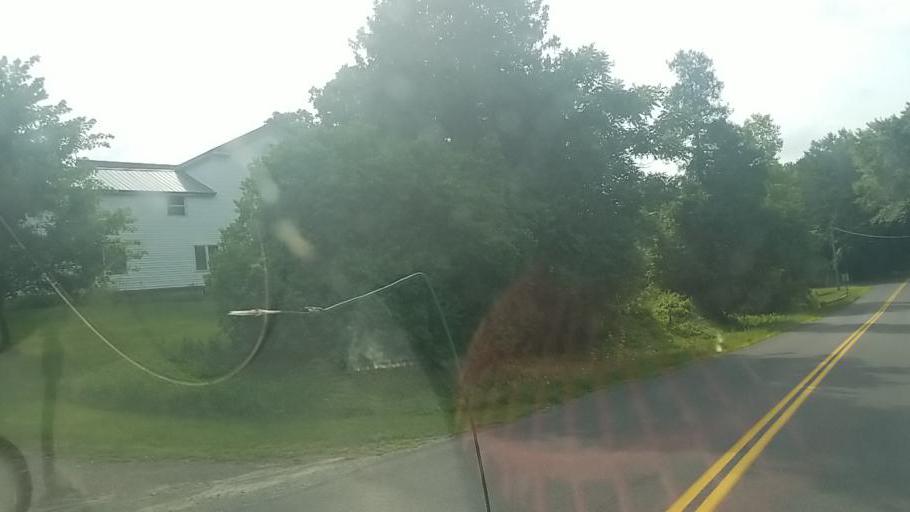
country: US
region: New York
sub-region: Fulton County
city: Johnstown
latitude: 43.0245
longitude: -74.3815
